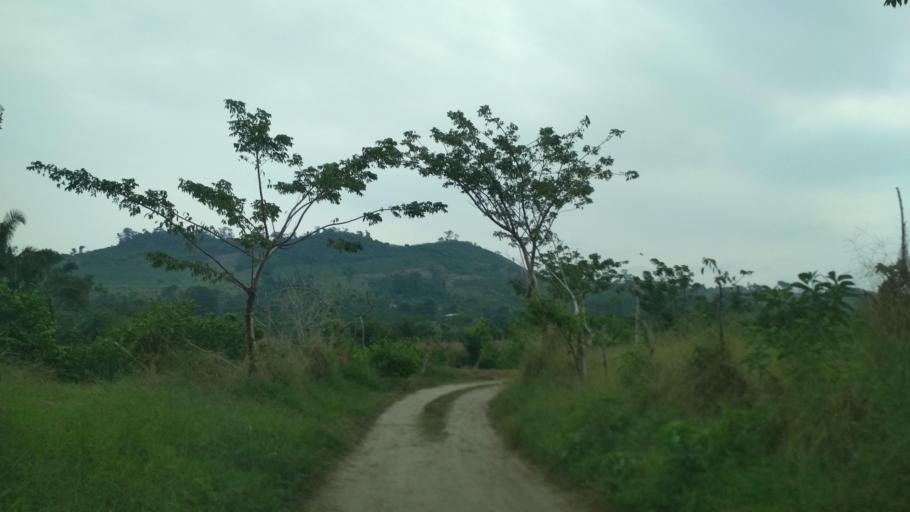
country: MM
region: Kayah
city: Loikaw
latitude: 20.2157
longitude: 97.3319
